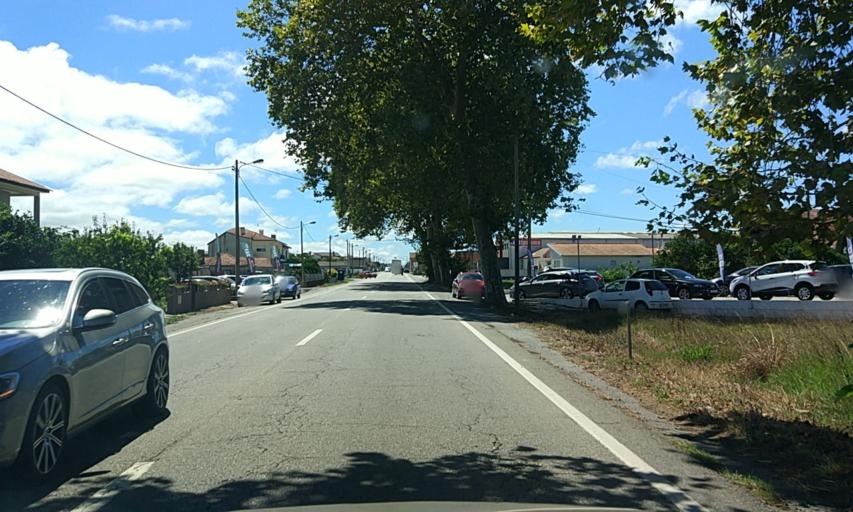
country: PT
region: Aveiro
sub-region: Vagos
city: Vagos
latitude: 40.4923
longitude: -8.6854
